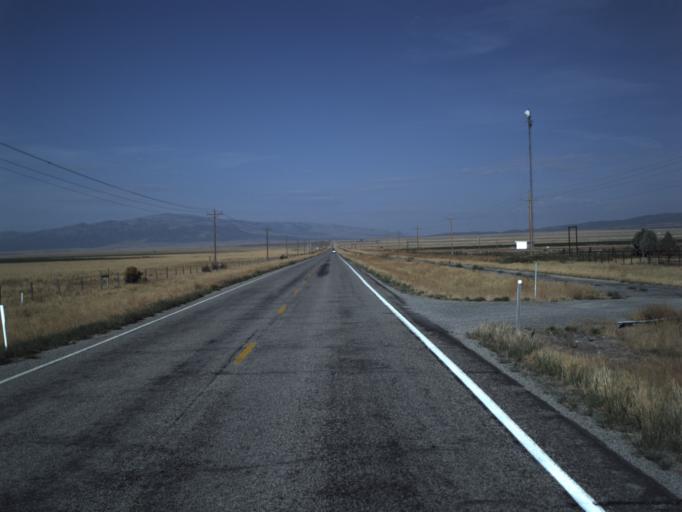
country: US
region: Idaho
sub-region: Oneida County
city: Malad City
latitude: 41.9664
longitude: -112.9270
